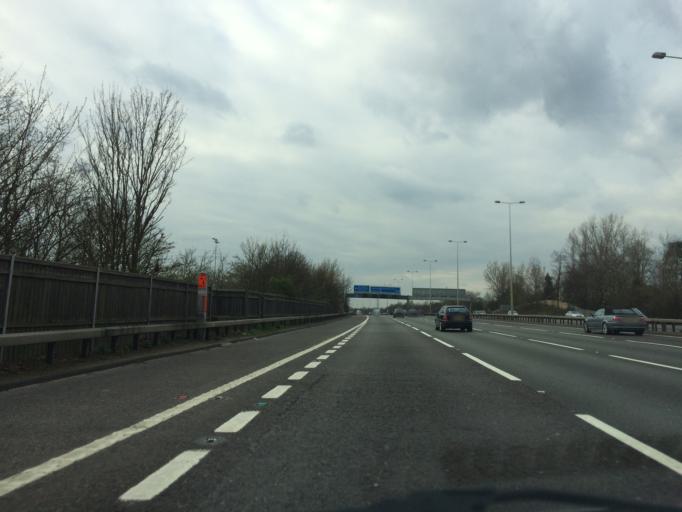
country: GB
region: England
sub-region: Surrey
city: Chertsey
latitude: 51.3819
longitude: -0.5151
